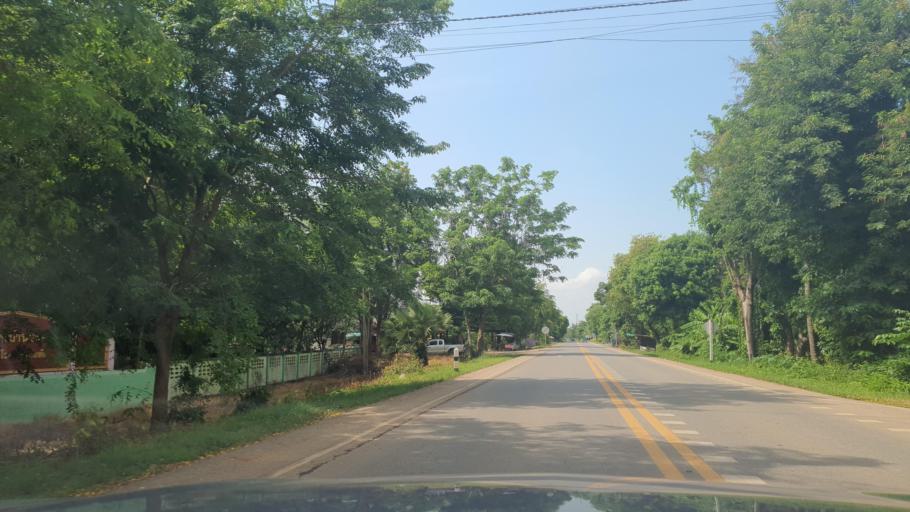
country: TH
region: Sukhothai
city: Si Samrong
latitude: 17.1471
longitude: 99.8242
